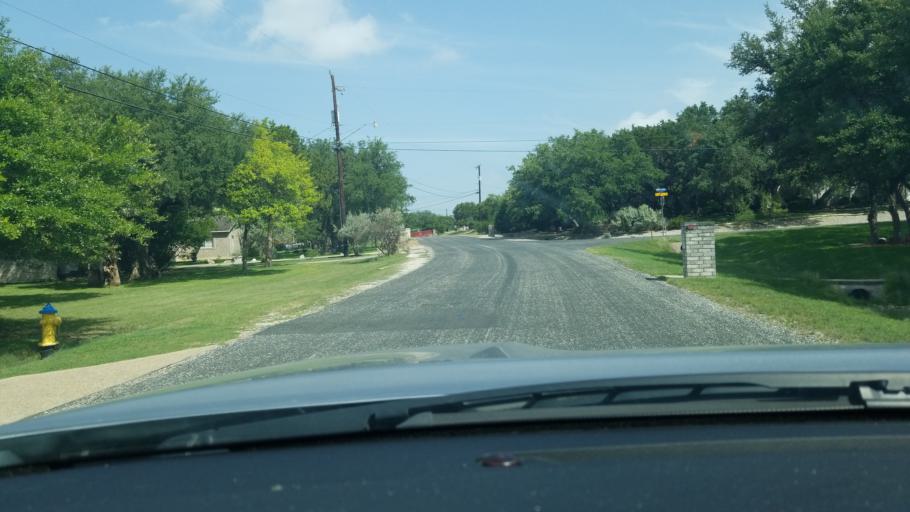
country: US
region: Texas
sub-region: Bexar County
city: Timberwood Park
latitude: 29.6916
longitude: -98.4941
